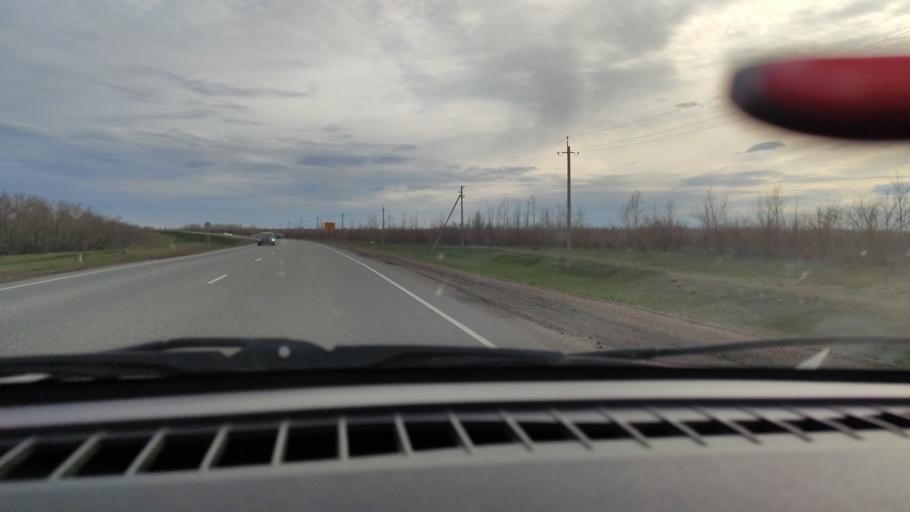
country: RU
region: Orenburg
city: Tatarskaya Kargala
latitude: 52.0157
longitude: 55.2069
